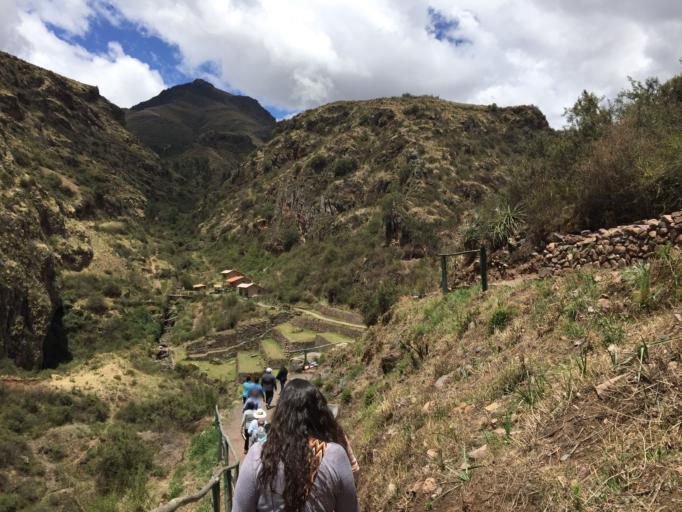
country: PE
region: Cusco
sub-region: Provincia de Calca
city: Pisac
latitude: -13.4080
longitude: -71.8448
